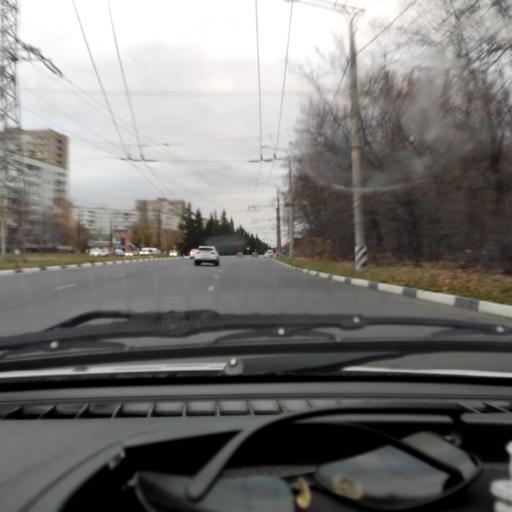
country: RU
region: Samara
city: Tol'yatti
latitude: 53.5045
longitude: 49.4323
